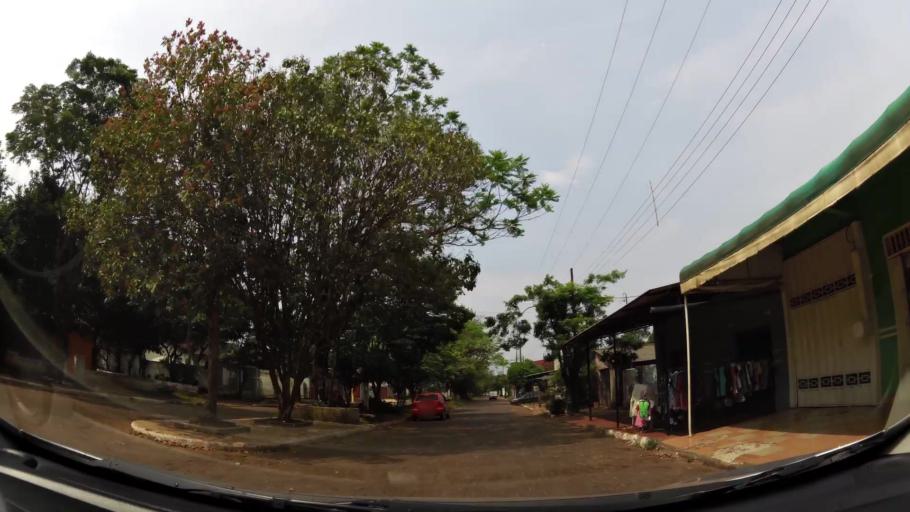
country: PY
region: Alto Parana
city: Presidente Franco
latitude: -25.5423
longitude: -54.6291
